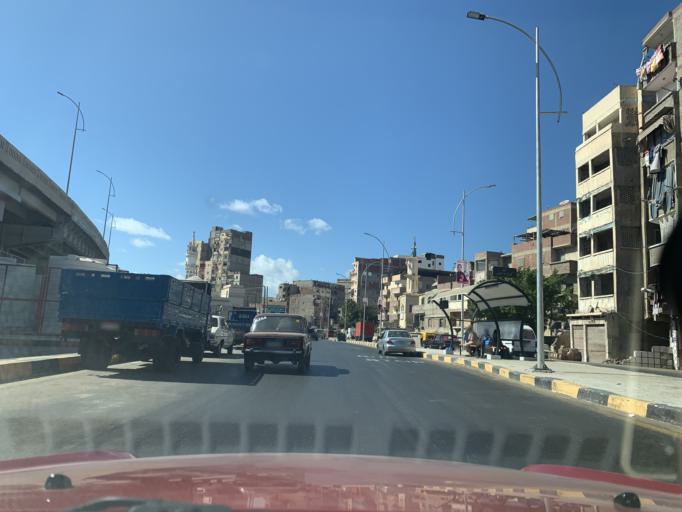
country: EG
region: Alexandria
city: Alexandria
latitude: 31.2249
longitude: 29.9809
